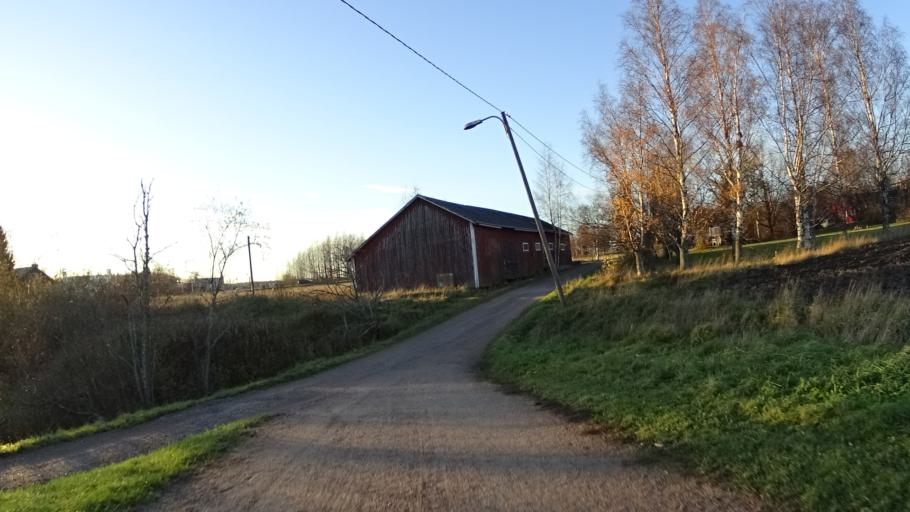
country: FI
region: Uusimaa
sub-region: Helsinki
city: Vantaa
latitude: 60.2802
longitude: 24.9842
